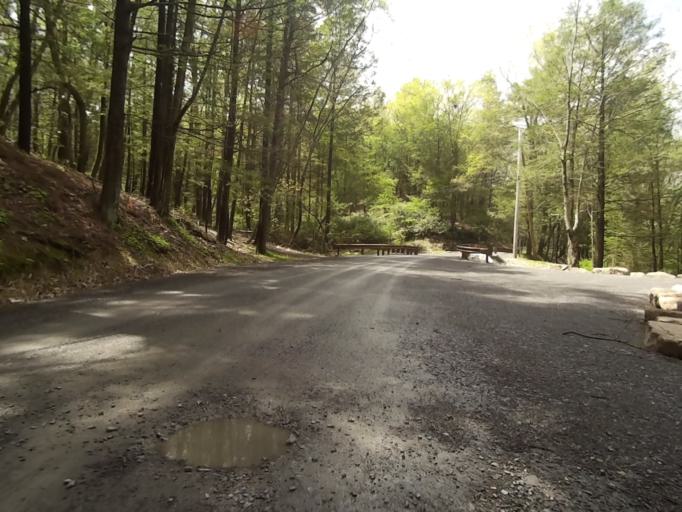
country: US
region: Pennsylvania
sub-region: Centre County
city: Boalsburg
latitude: 40.7625
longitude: -77.7519
